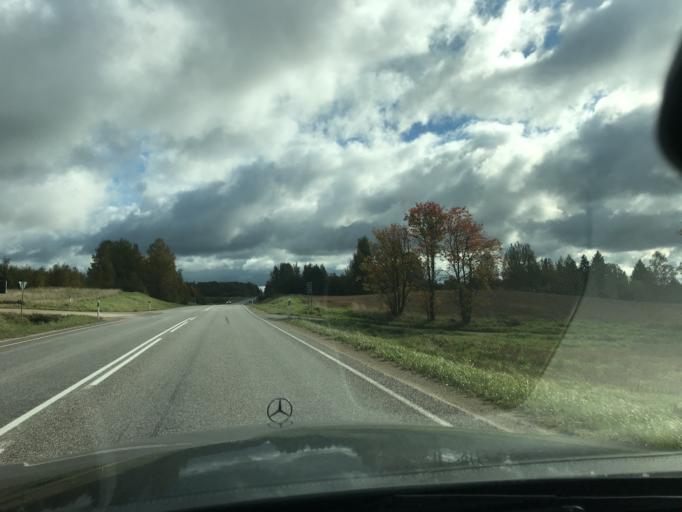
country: EE
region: Vorumaa
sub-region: Voru linn
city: Voru
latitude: 57.7620
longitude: 27.2018
